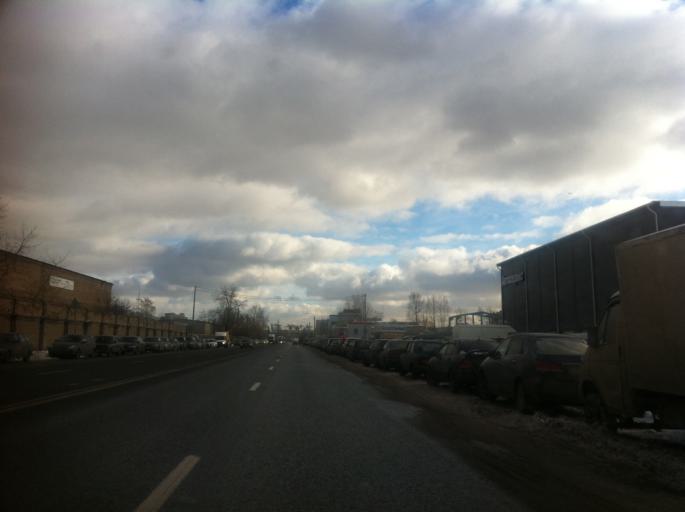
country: RU
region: St.-Petersburg
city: Avtovo
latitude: 59.8709
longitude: 30.2304
